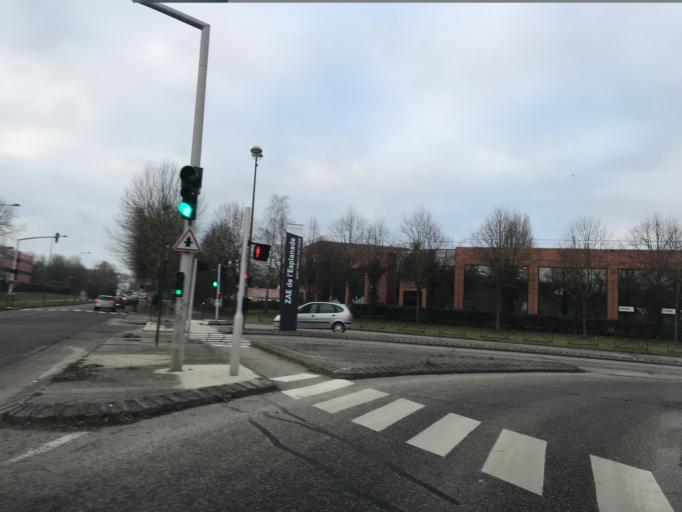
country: FR
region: Ile-de-France
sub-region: Departement de Seine-et-Marne
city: Saint-Thibault-des-Vignes
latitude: 48.8633
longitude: 2.6752
